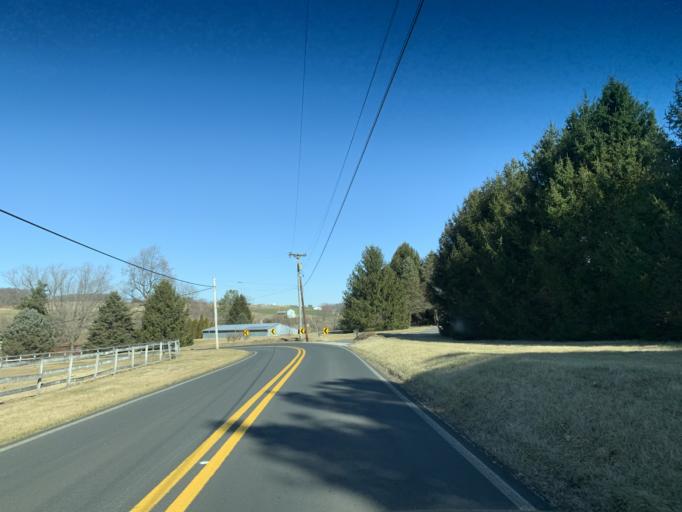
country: US
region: Maryland
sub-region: Carroll County
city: Manchester
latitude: 39.6222
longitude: -76.8921
